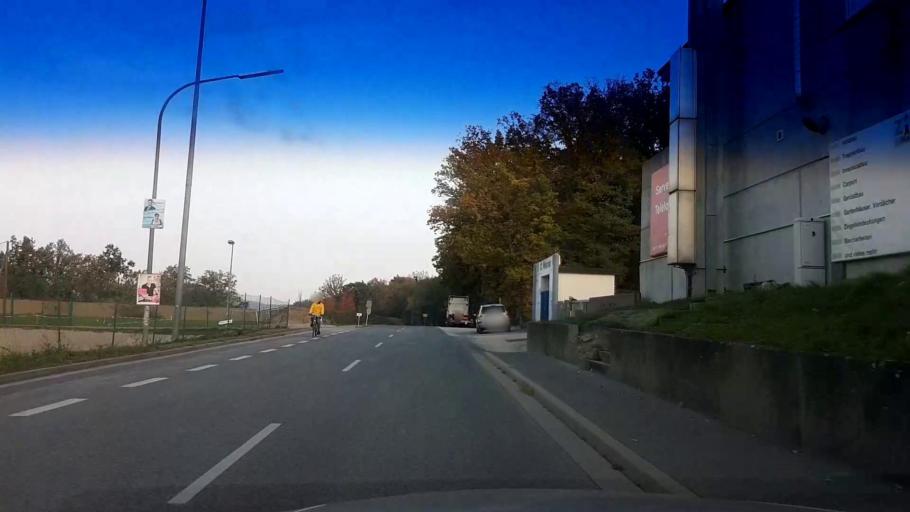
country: DE
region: Bavaria
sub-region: Upper Franconia
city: Weismain
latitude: 50.0895
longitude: 11.2480
